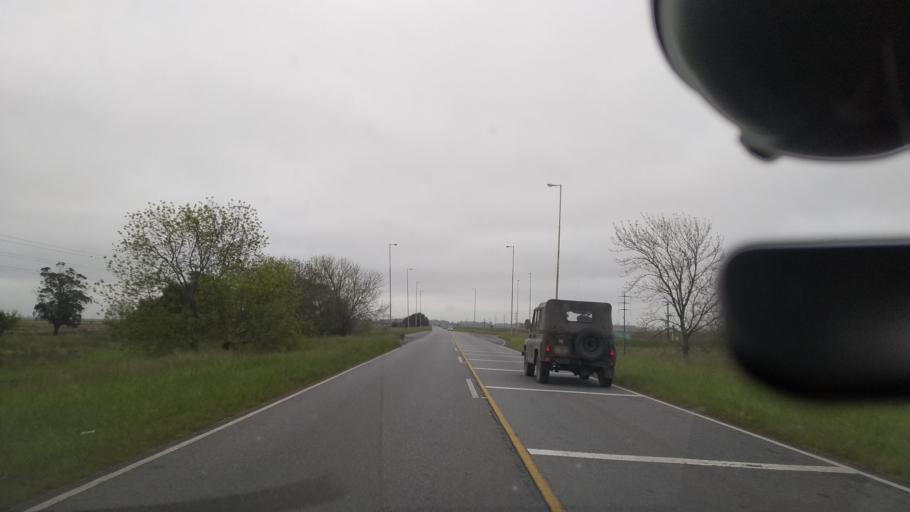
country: AR
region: Buenos Aires
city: Veronica
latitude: -35.3632
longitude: -57.3975
